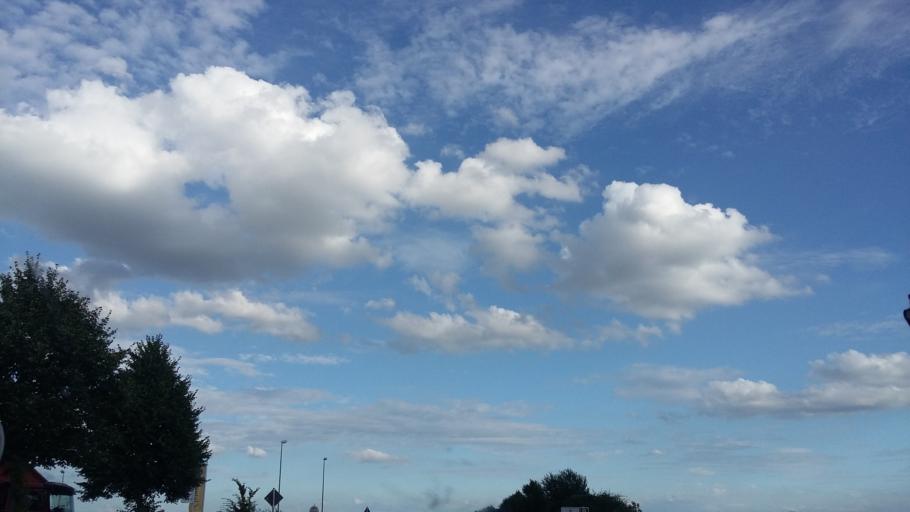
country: DE
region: Bavaria
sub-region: Swabia
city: Merching
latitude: 48.2455
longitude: 10.9933
